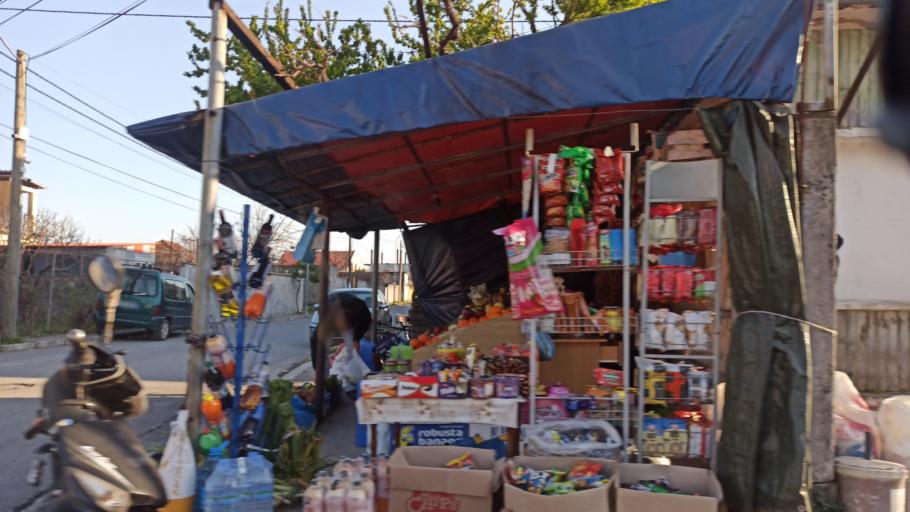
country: AL
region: Shkoder
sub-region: Rrethi i Shkodres
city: Shkoder
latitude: 42.0784
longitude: 19.5004
